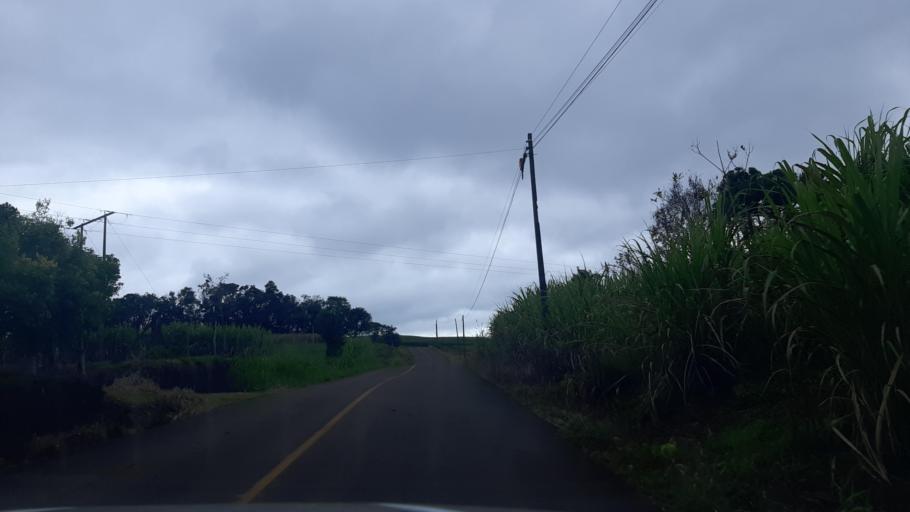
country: BR
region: Parana
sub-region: Ampere
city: Ampere
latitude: -26.0394
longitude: -53.4913
